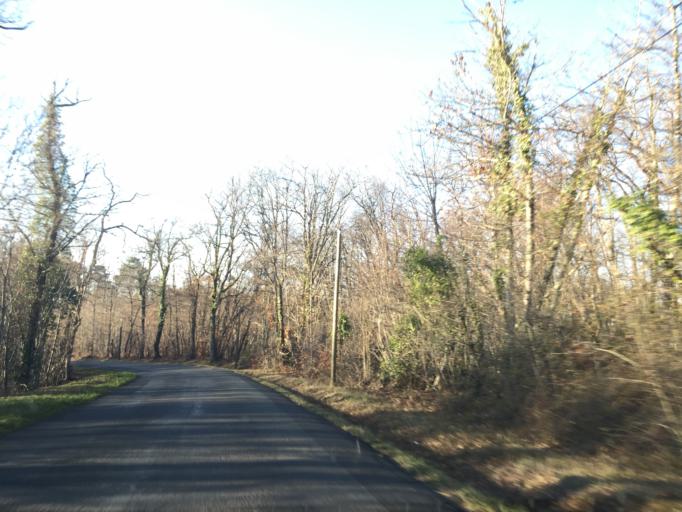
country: FR
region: Aquitaine
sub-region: Departement de la Dordogne
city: Riberac
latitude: 45.2042
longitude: 0.3543
